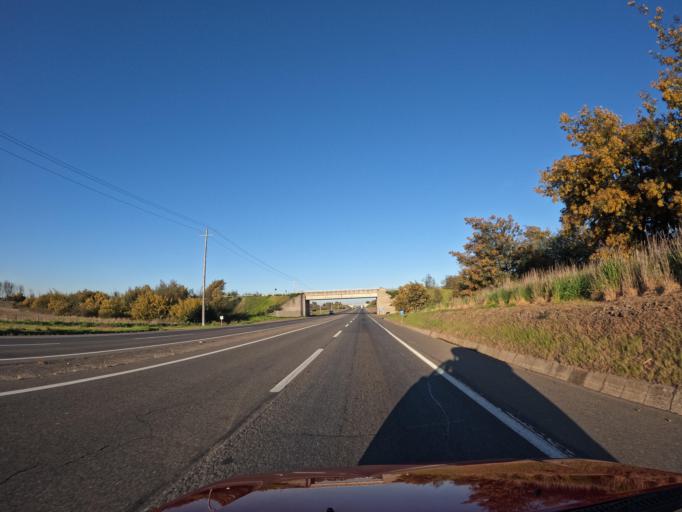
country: CL
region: Biobio
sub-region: Provincia de Nuble
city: Bulnes
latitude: -36.6588
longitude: -72.2847
